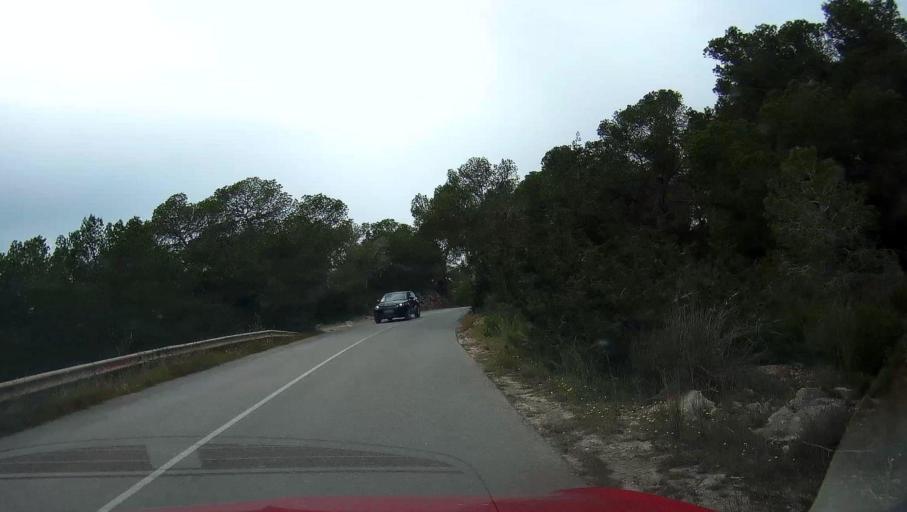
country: ES
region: Balearic Islands
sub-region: Illes Balears
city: Sant Josep de sa Talaia
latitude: 38.8690
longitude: 1.3366
